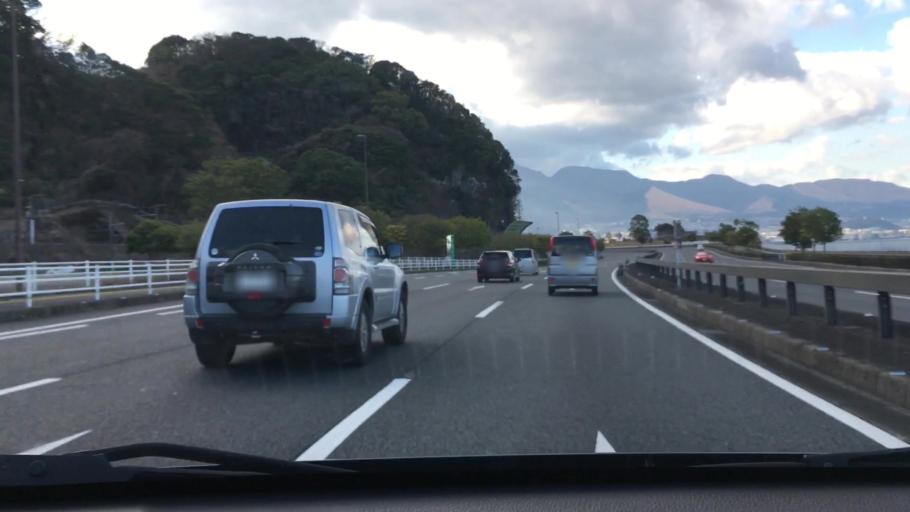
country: JP
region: Oita
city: Oita
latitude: 33.2560
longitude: 131.5565
